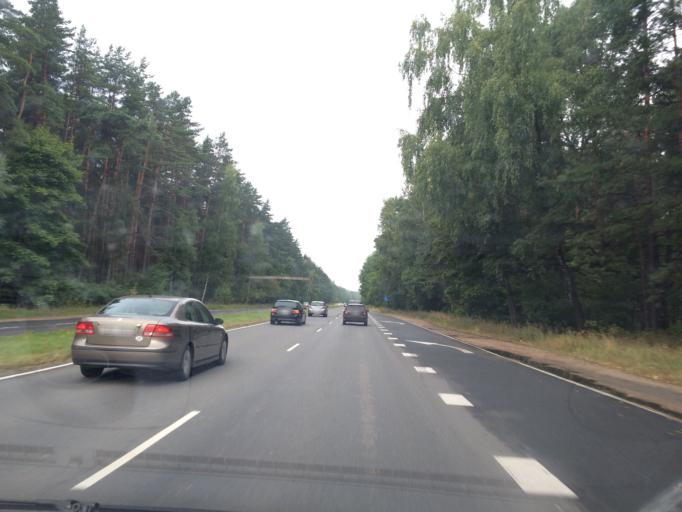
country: LV
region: Salaspils
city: Salaspils
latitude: 56.8612
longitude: 24.3024
